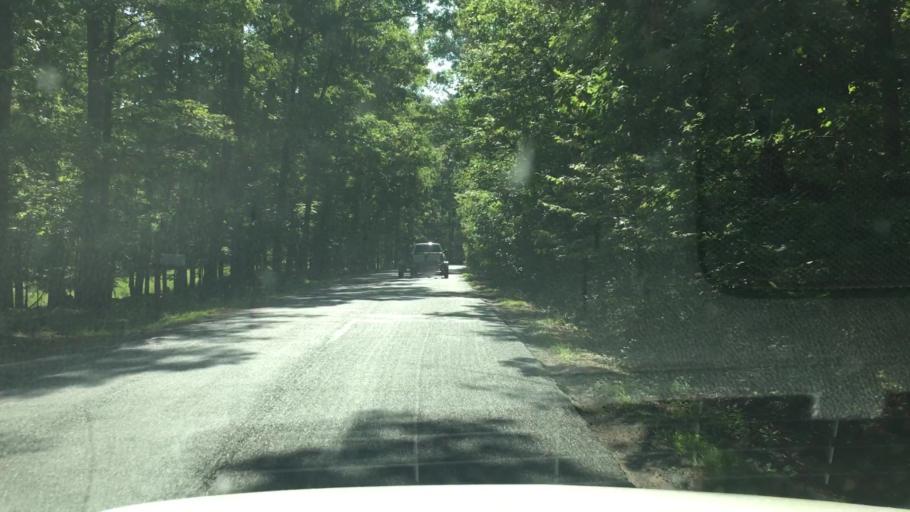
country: US
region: Arkansas
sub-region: Garland County
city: Piney
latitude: 34.5420
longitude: -93.3545
